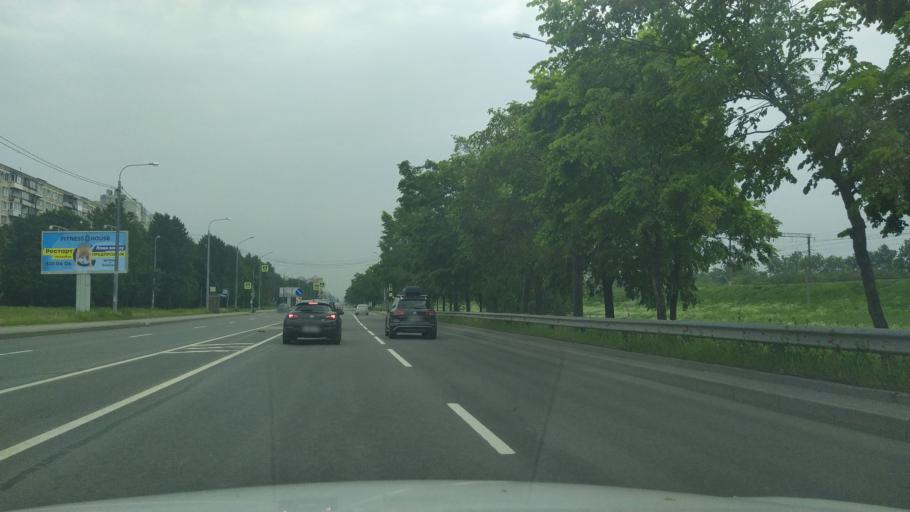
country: RU
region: St.-Petersburg
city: Kupchino
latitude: 59.8727
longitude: 30.3565
